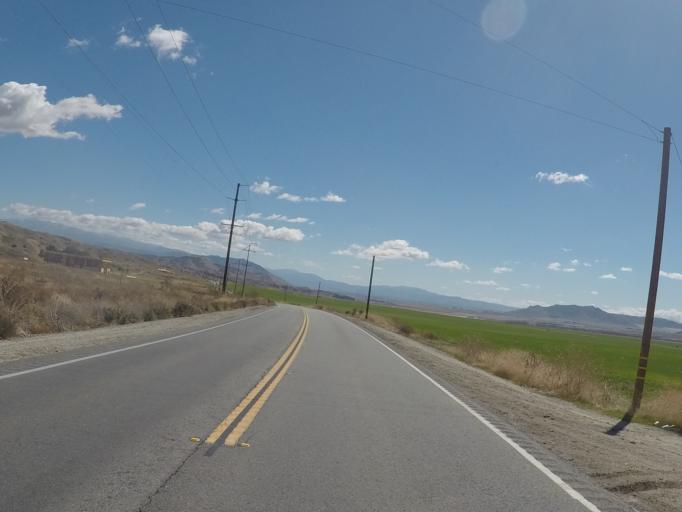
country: US
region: California
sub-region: Riverside County
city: Lakeview
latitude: 33.9286
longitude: -117.1212
